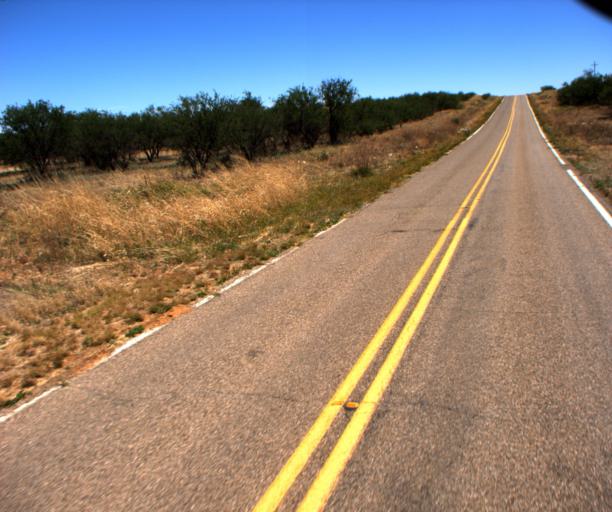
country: US
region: Arizona
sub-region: Pima County
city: Sells
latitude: 31.5667
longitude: -111.5384
